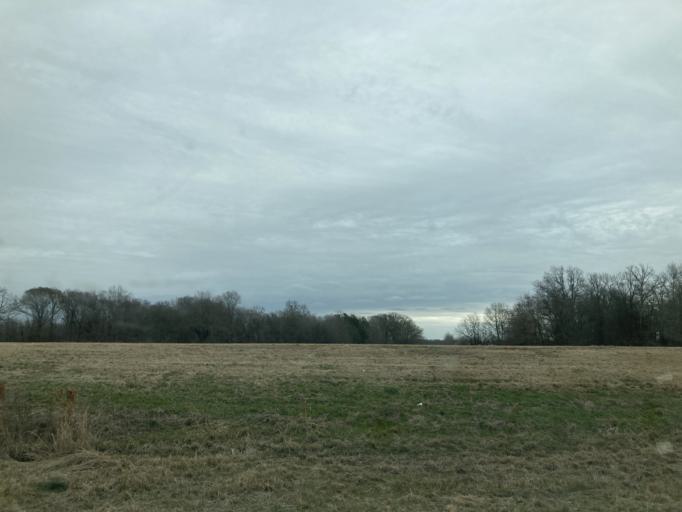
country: US
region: Mississippi
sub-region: Yazoo County
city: Yazoo City
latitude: 32.9970
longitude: -90.4703
